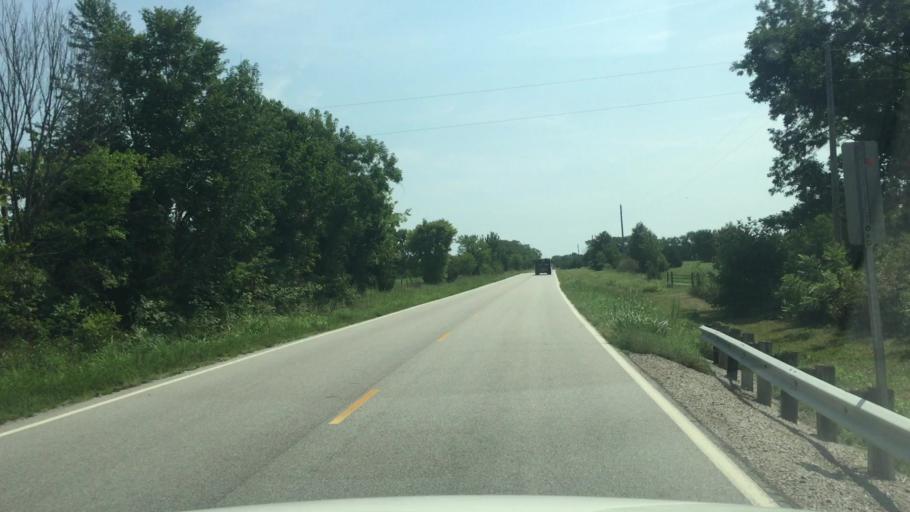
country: US
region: Kansas
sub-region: Montgomery County
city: Cherryvale
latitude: 37.1940
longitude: -95.5486
